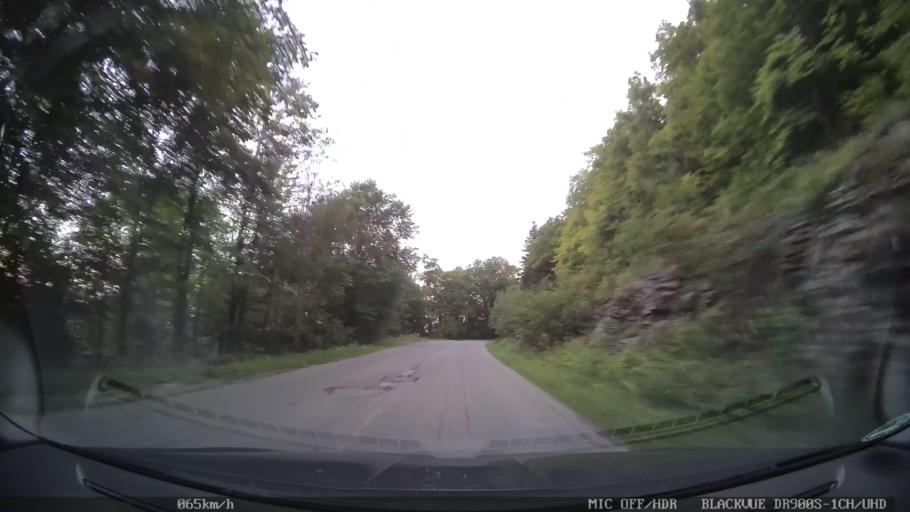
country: HR
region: Primorsko-Goranska
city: Novi Vinodolski
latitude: 45.1795
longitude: 14.9871
